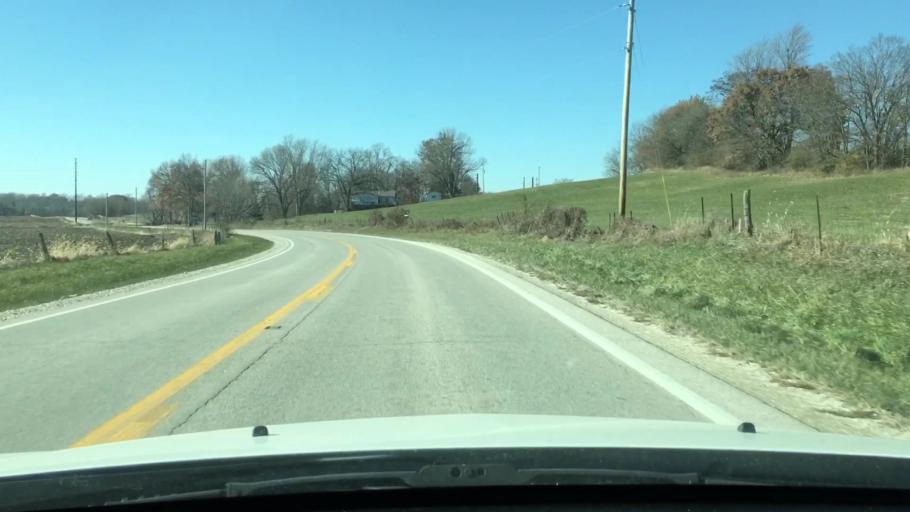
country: US
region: Illinois
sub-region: Pike County
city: Pittsfield
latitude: 39.6127
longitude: -90.7488
